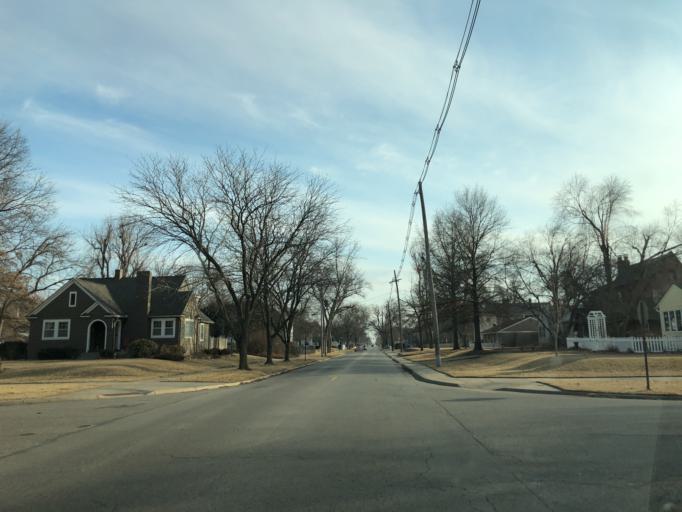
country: US
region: Kansas
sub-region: Reno County
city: Hutchinson
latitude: 38.0754
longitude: -97.9355
